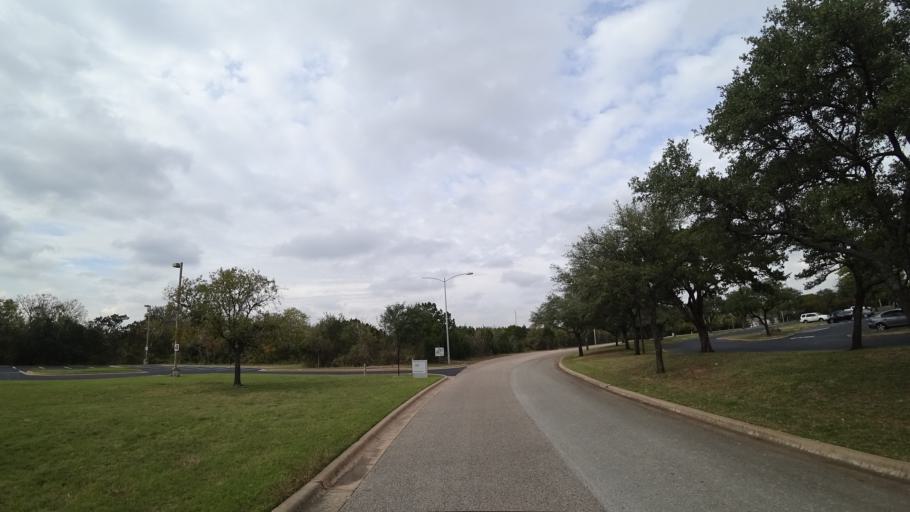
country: US
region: Texas
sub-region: Travis County
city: Wells Branch
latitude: 30.4469
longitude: -97.6931
